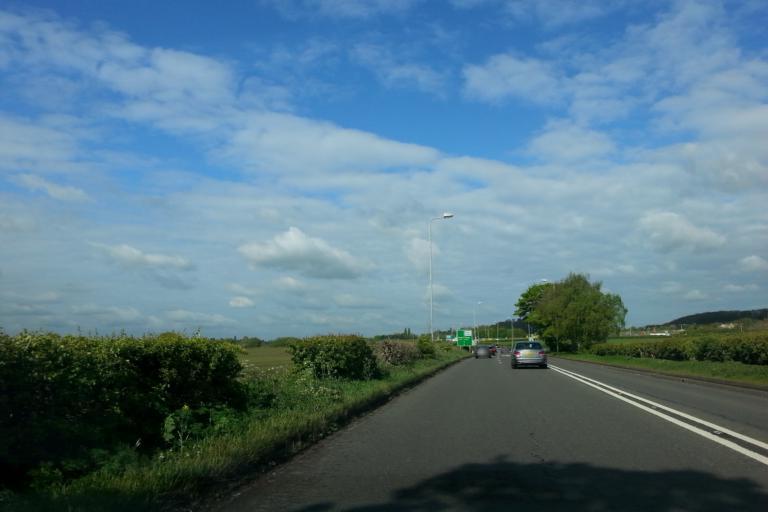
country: GB
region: England
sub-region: Nottinghamshire
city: West Bridgford
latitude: 52.9010
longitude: -1.1103
